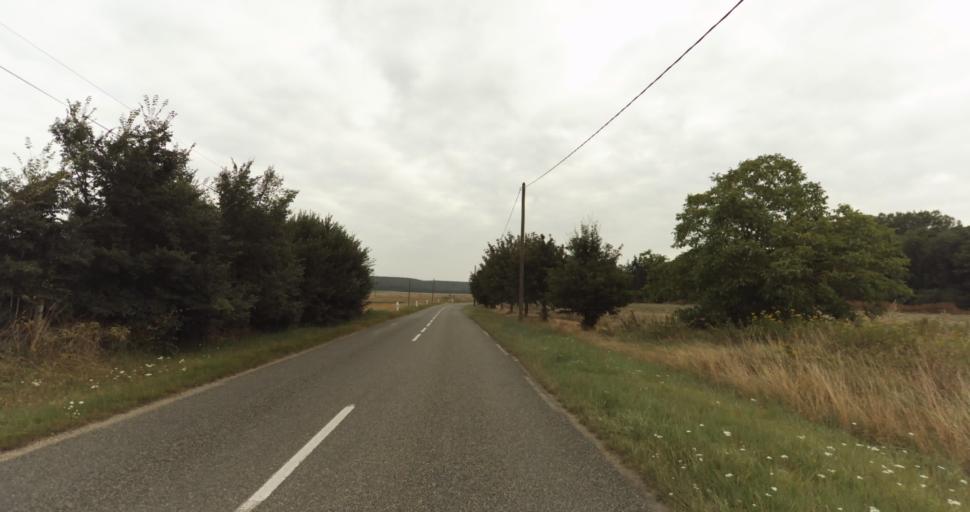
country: FR
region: Haute-Normandie
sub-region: Departement de l'Eure
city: Marcilly-sur-Eure
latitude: 48.8324
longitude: 1.3491
